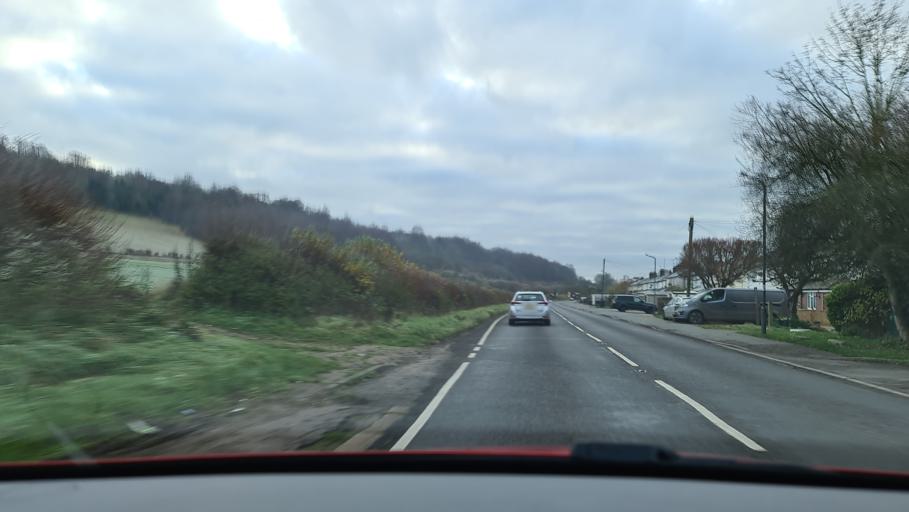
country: GB
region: England
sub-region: Buckinghamshire
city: High Wycombe
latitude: 51.6587
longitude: -0.8036
